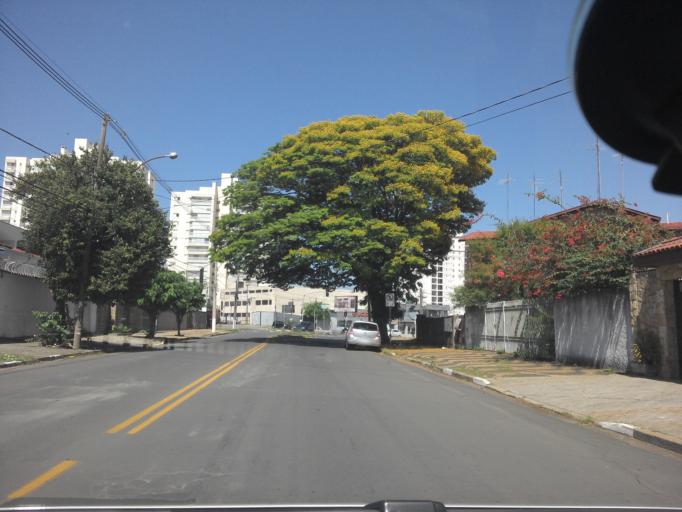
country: BR
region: Sao Paulo
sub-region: Campinas
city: Campinas
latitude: -22.8815
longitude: -47.0600
